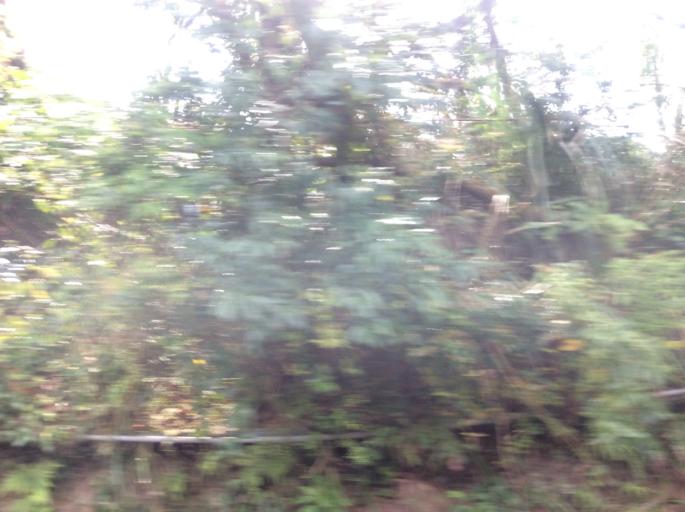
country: TW
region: Taipei
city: Taipei
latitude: 25.1622
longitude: 121.5441
